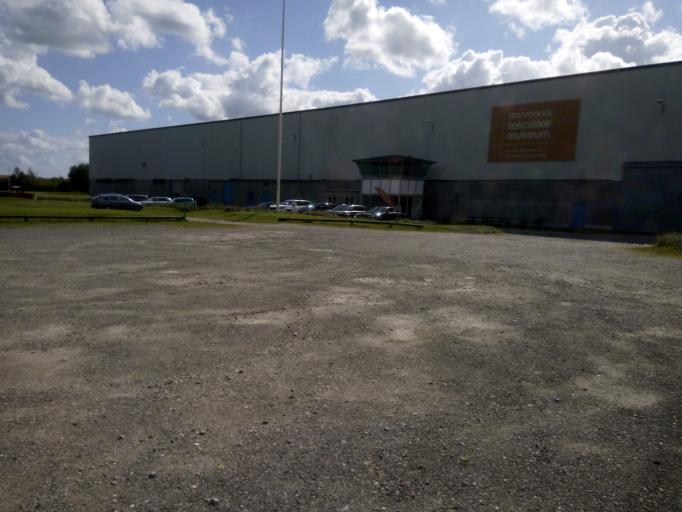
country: DK
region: Capital Region
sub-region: Helsingor Kommune
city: Espergaerde
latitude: 56.0228
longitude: 12.5634
